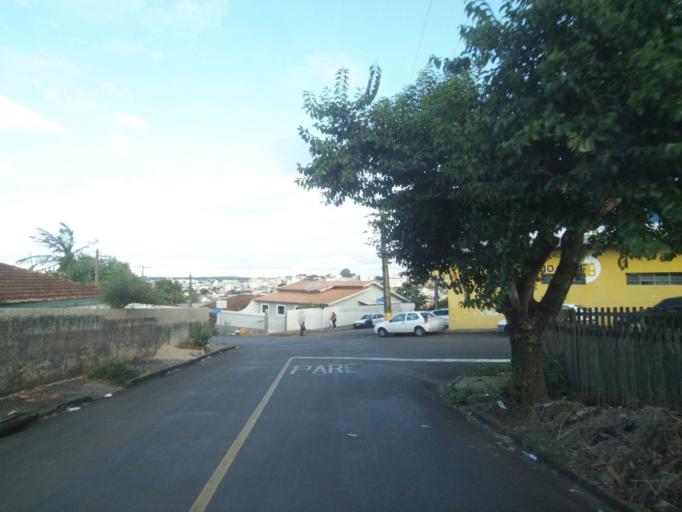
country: BR
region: Parana
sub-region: Telemaco Borba
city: Telemaco Borba
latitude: -24.3277
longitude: -50.6362
